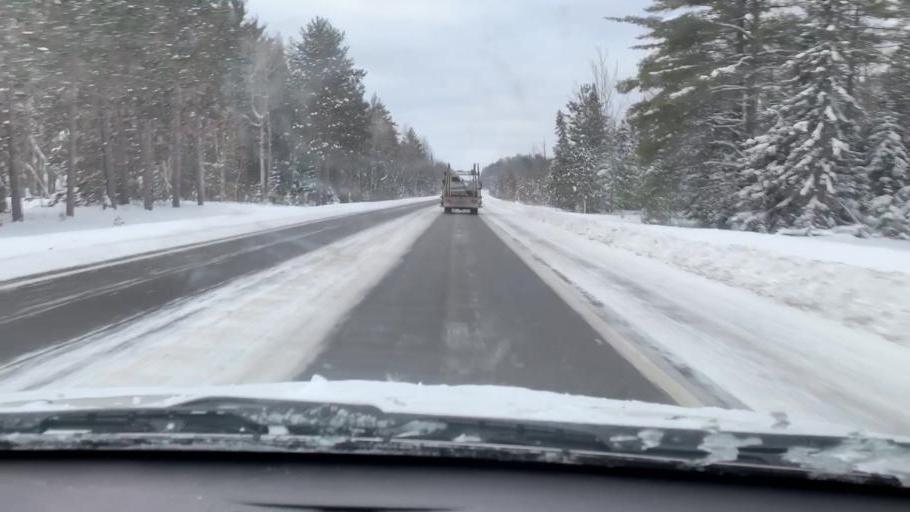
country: US
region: Michigan
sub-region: Kalkaska County
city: Kalkaska
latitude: 44.6997
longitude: -85.2048
